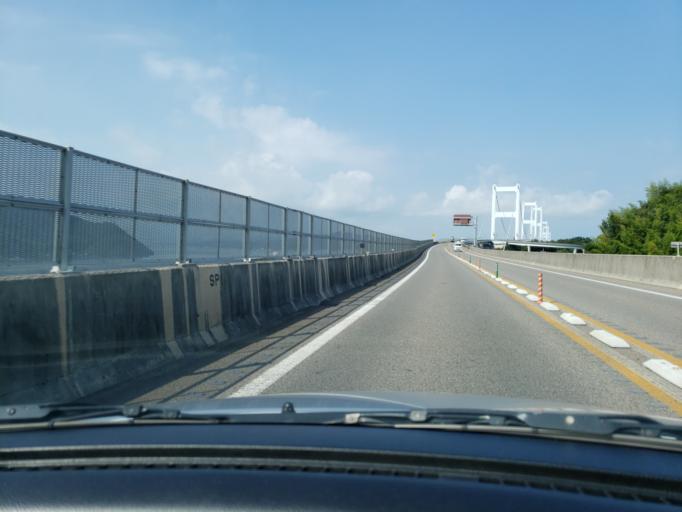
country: JP
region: Hiroshima
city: Innoshima
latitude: 34.1299
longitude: 133.0216
